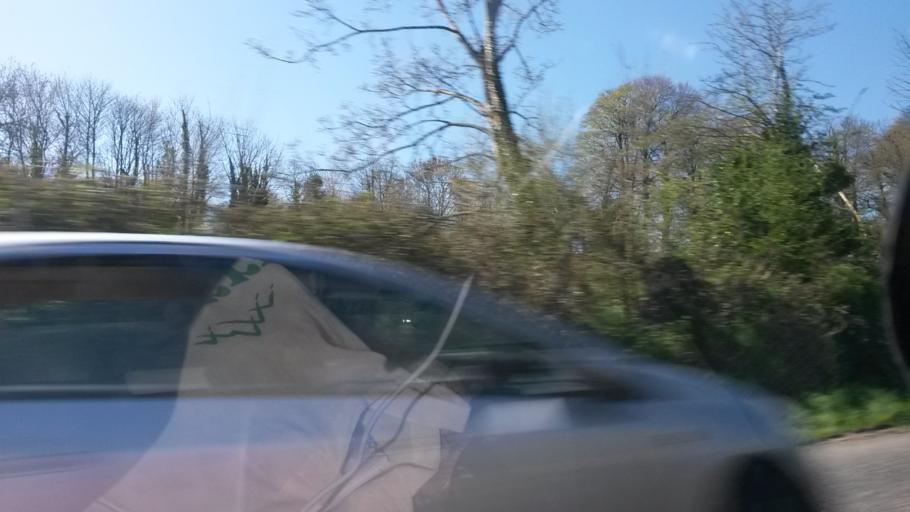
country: IE
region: Munster
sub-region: County Cork
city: Blarney
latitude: 51.8970
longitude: -8.5541
